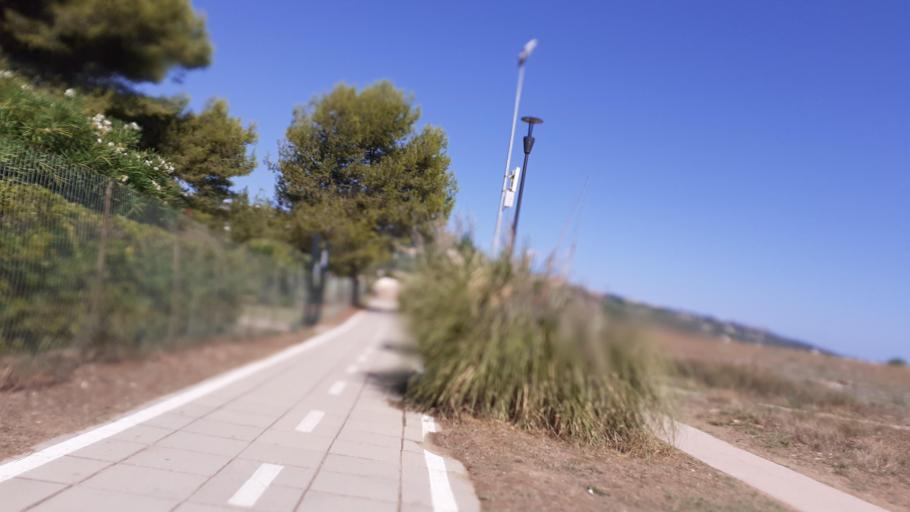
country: IT
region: Abruzzo
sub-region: Provincia di Chieti
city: Marina di Vasto
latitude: 42.0944
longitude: 14.7278
